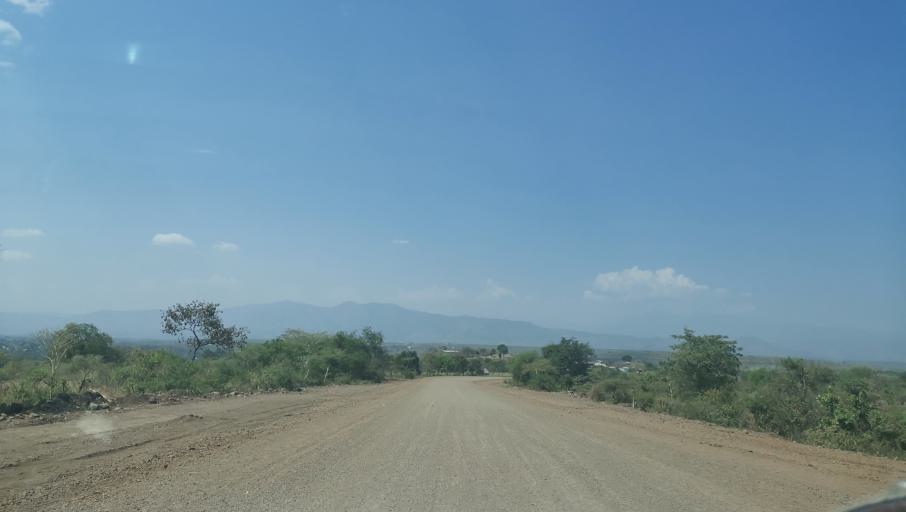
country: ET
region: Southern Nations, Nationalities, and People's Region
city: Arba Minch'
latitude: 6.3390
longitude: 37.3221
